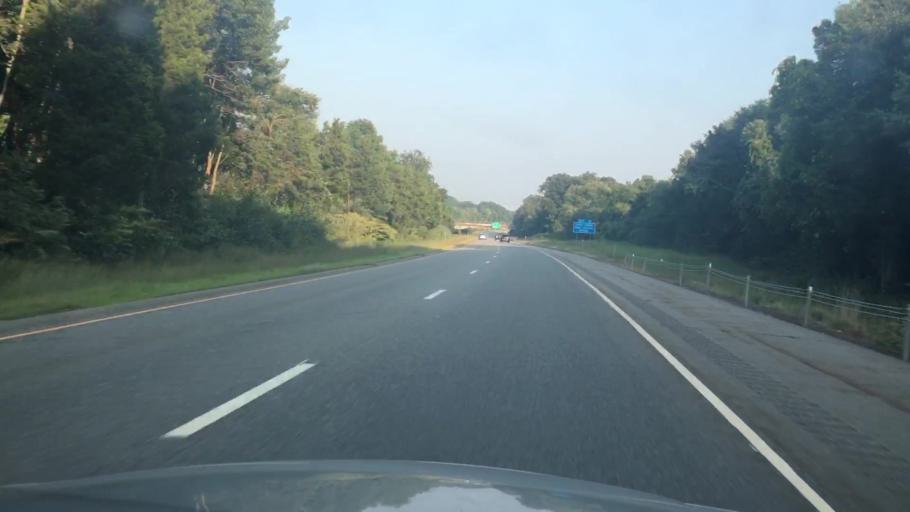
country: US
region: Connecticut
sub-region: Middlesex County
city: Essex Village
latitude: 41.3559
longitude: -72.4142
